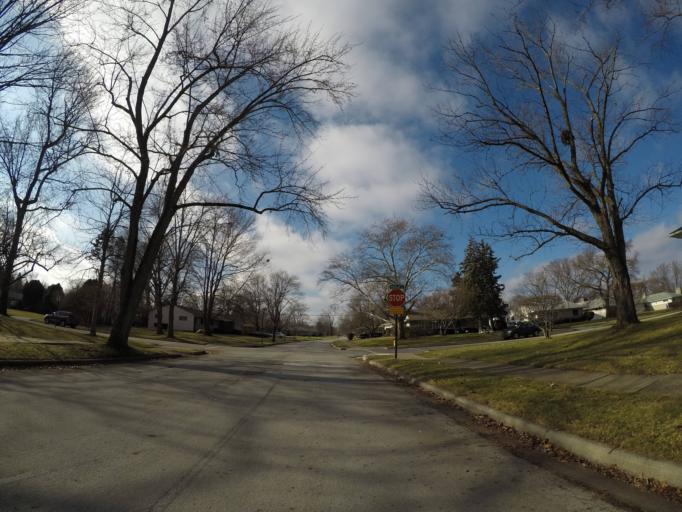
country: US
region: Ohio
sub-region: Franklin County
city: Upper Arlington
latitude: 40.0264
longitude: -83.0637
